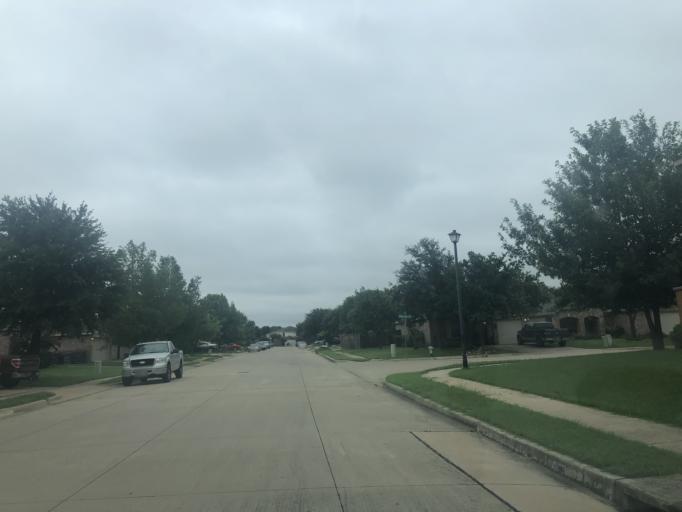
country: US
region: Texas
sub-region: Dallas County
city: Dallas
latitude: 32.7908
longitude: -96.8645
